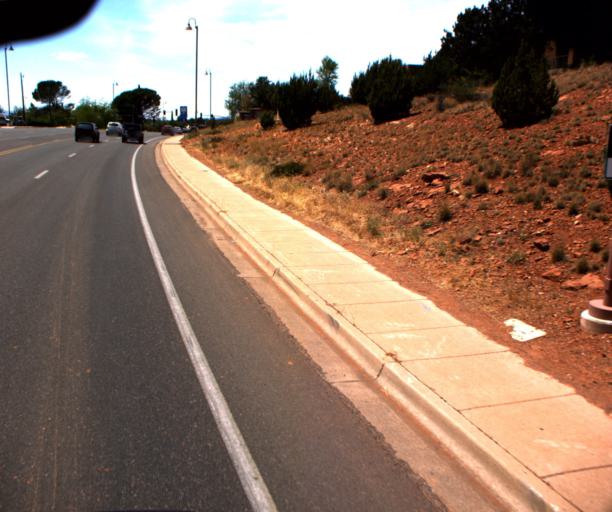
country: US
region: Arizona
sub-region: Coconino County
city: Sedona
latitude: 34.8626
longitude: -111.7810
